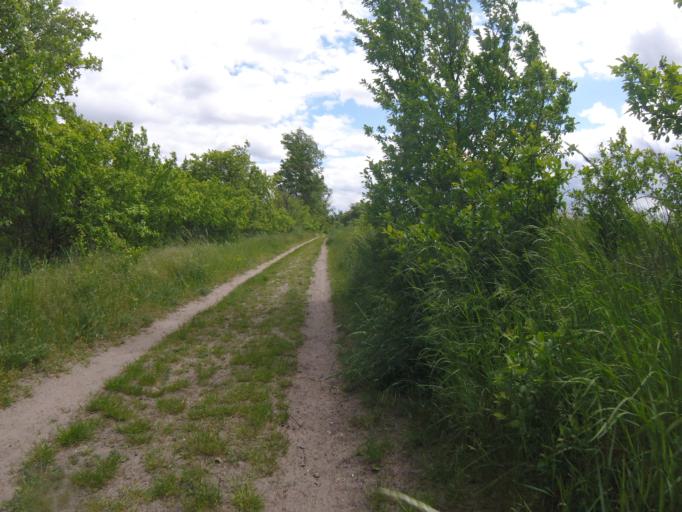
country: DE
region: Brandenburg
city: Mittenwalde
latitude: 52.2577
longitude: 13.5584
